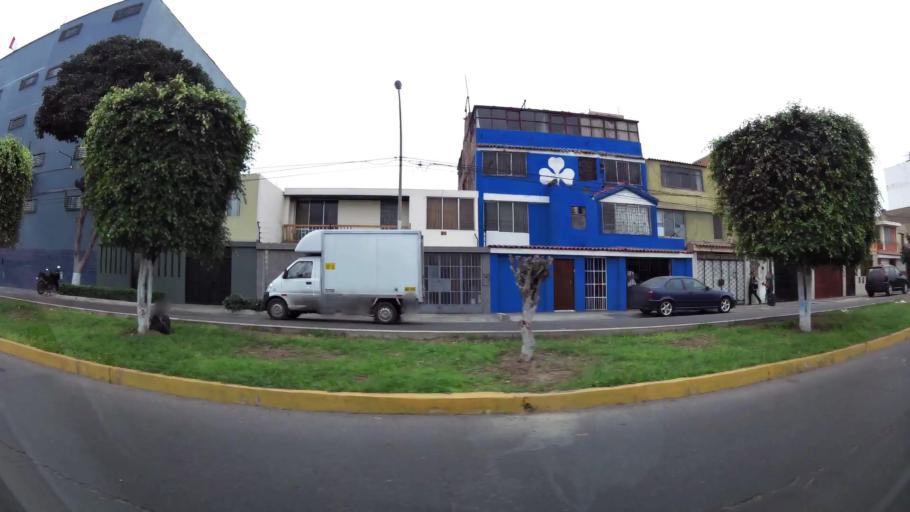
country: PE
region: Callao
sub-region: Callao
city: Callao
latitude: -12.0629
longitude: -77.1026
